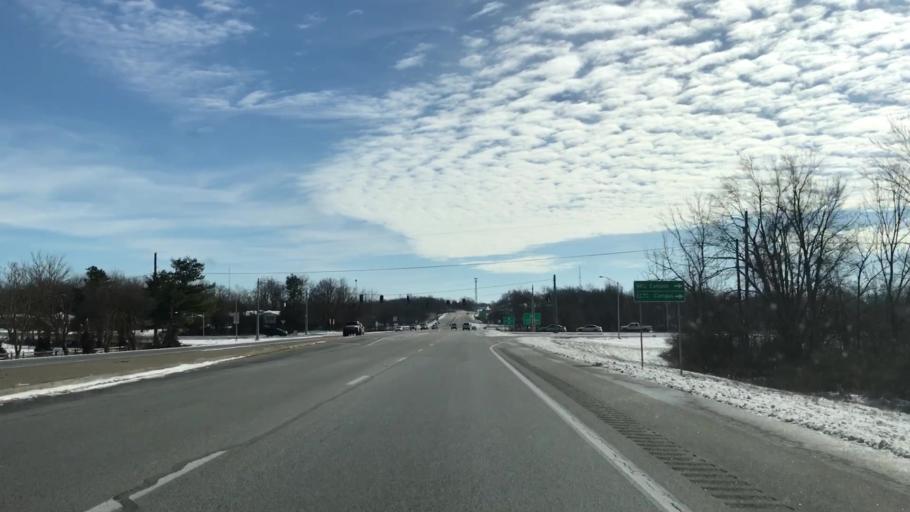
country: US
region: Kentucky
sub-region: Hardin County
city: Elizabethtown
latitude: 37.6929
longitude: -85.8735
